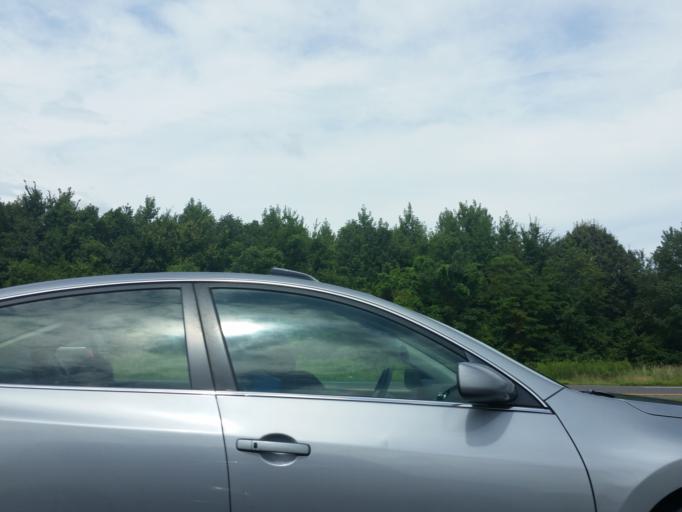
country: US
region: Kentucky
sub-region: McCracken County
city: Hendron
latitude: 37.0286
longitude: -88.6165
